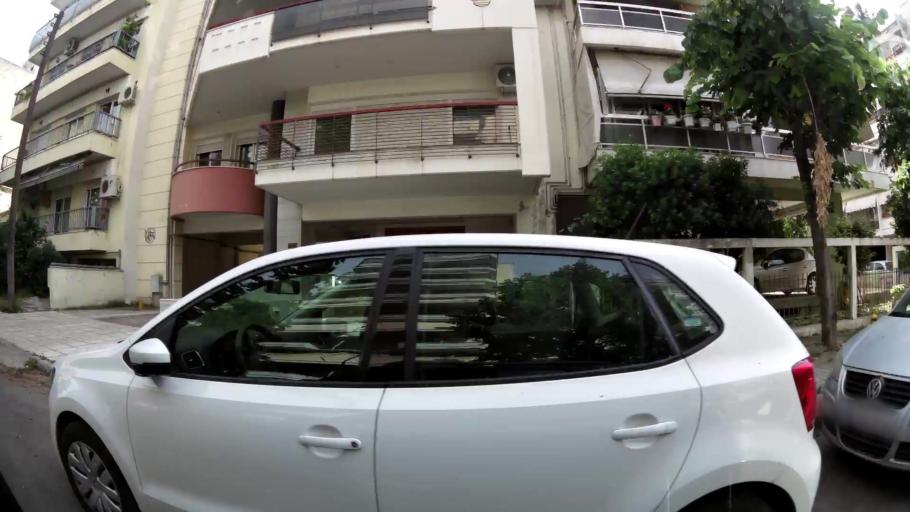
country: GR
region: Central Macedonia
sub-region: Nomos Thessalonikis
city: Kalamaria
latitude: 40.5857
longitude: 22.9583
